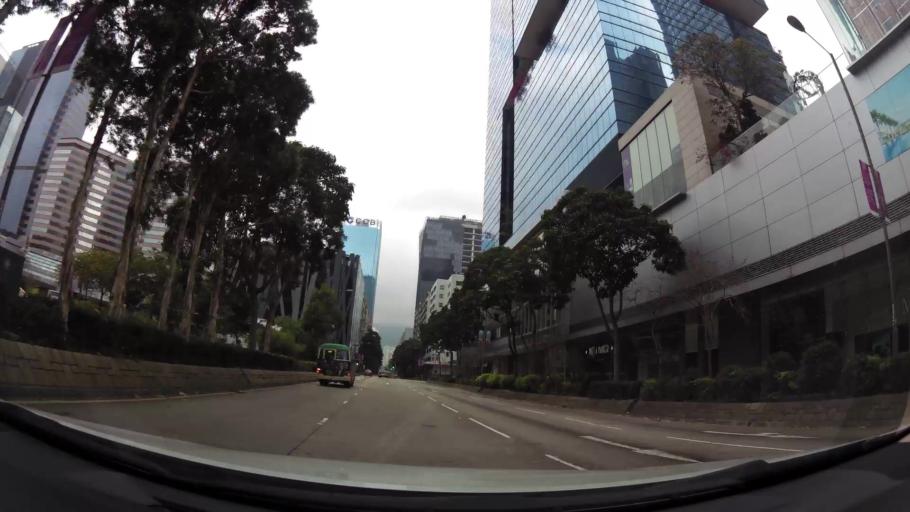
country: HK
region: Kowloon City
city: Kowloon
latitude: 22.3207
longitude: 114.2090
